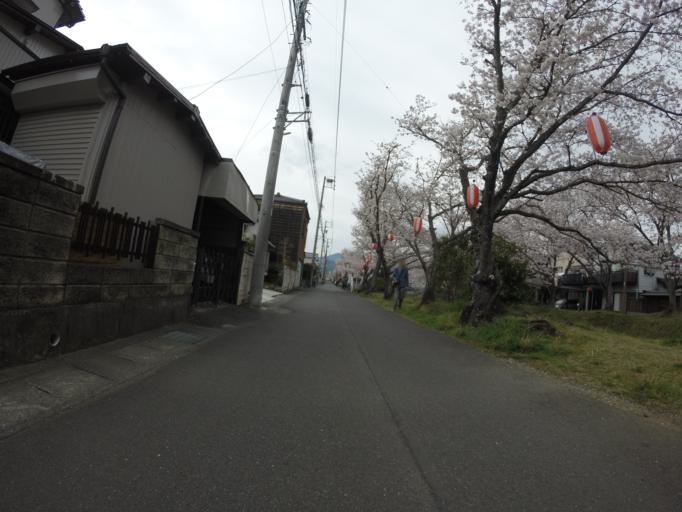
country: JP
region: Shizuoka
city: Shizuoka-shi
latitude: 35.0073
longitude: 138.4720
